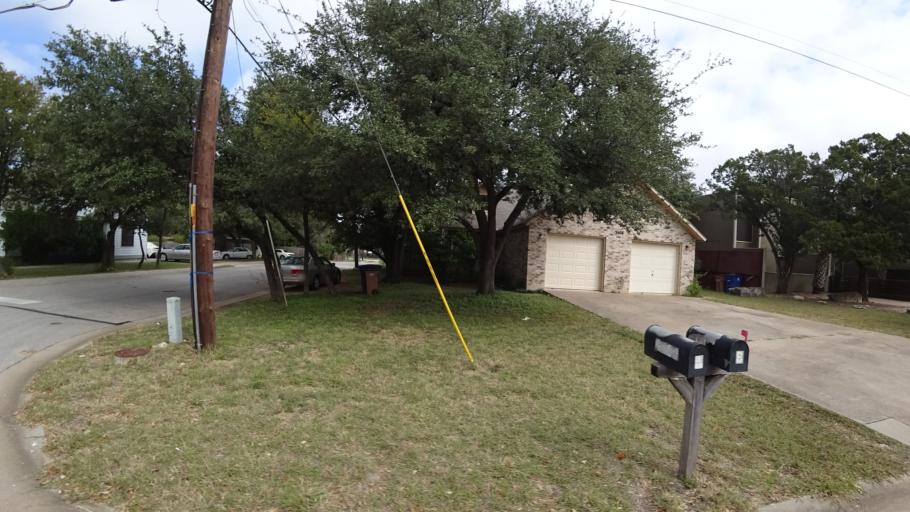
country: US
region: Texas
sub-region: Travis County
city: Shady Hollow
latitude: 30.2041
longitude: -97.8343
